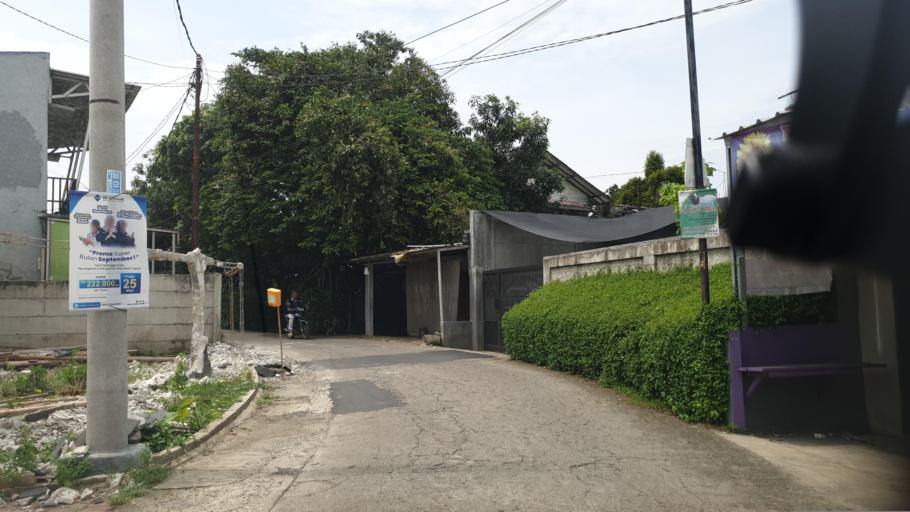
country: ID
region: West Java
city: Sawangan
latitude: -6.3754
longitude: 106.7602
